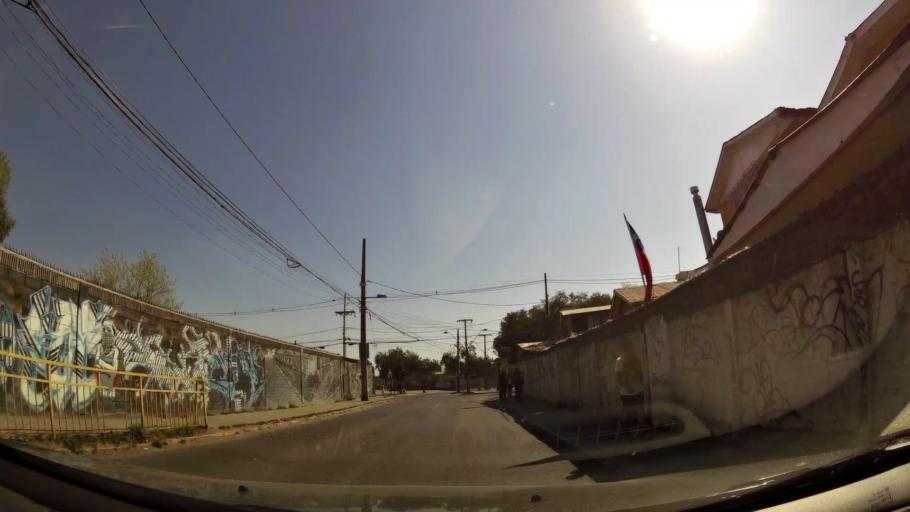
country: CL
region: Santiago Metropolitan
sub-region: Provincia de Santiago
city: La Pintana
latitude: -33.6263
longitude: -70.6240
